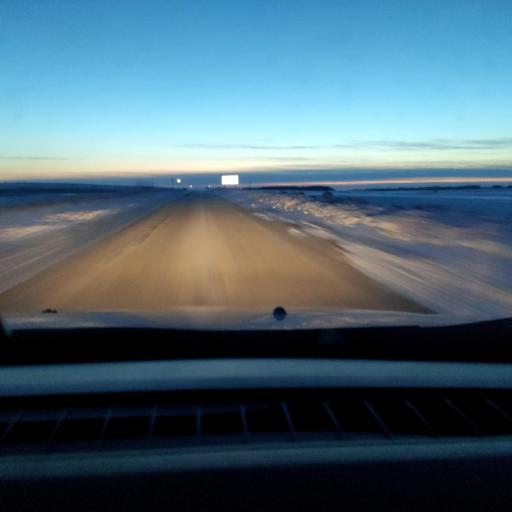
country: RU
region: Samara
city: Georgiyevka
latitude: 53.3075
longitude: 50.8169
